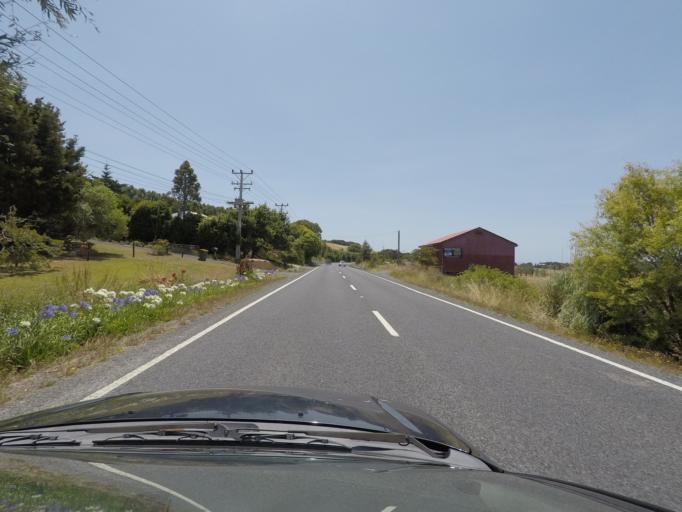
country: NZ
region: Auckland
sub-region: Auckland
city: Warkworth
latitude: -36.3820
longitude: 174.6623
